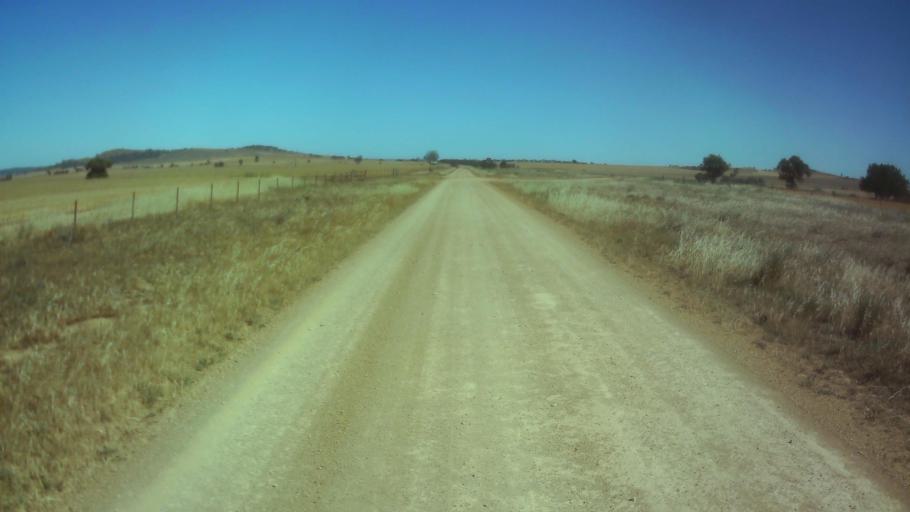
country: AU
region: New South Wales
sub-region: Weddin
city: Grenfell
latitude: -33.9799
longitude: 148.3273
